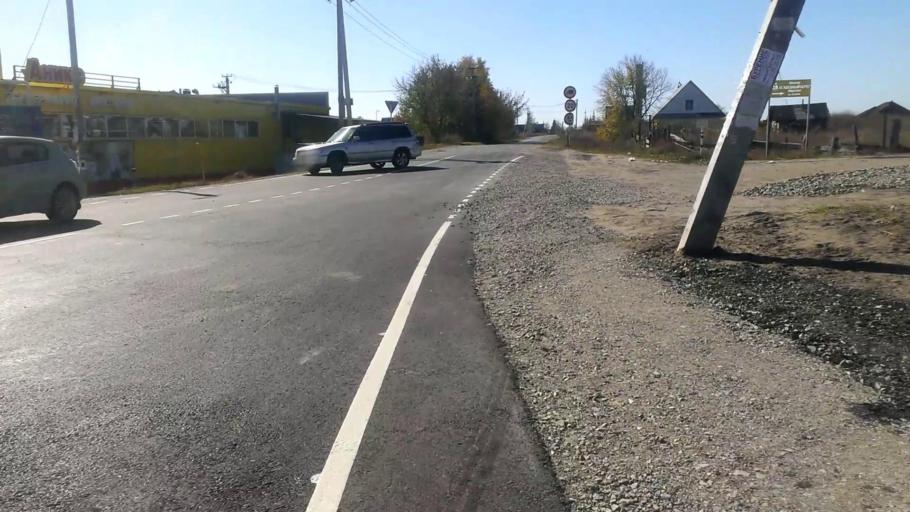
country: RU
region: Altai Krai
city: Sannikovo
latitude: 53.3187
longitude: 83.9443
